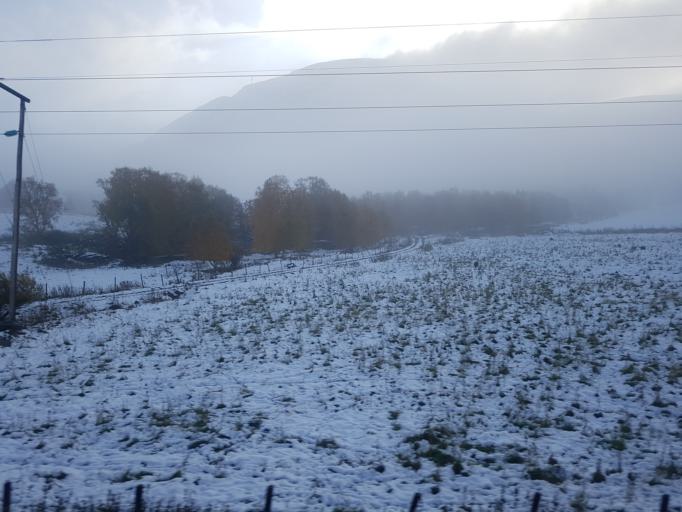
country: NO
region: Sor-Trondelag
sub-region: Oppdal
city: Oppdal
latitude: 62.5675
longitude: 9.6454
